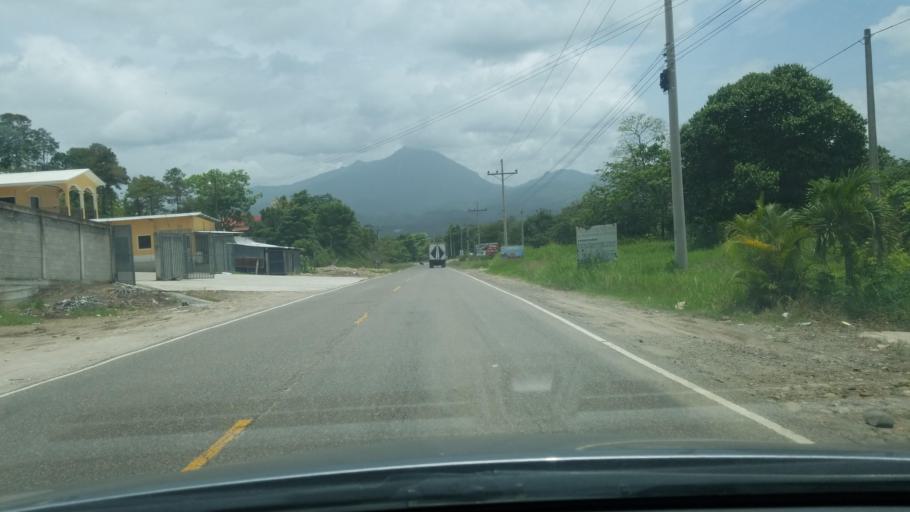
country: HN
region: Copan
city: Cucuyagua
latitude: 14.6691
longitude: -88.8606
